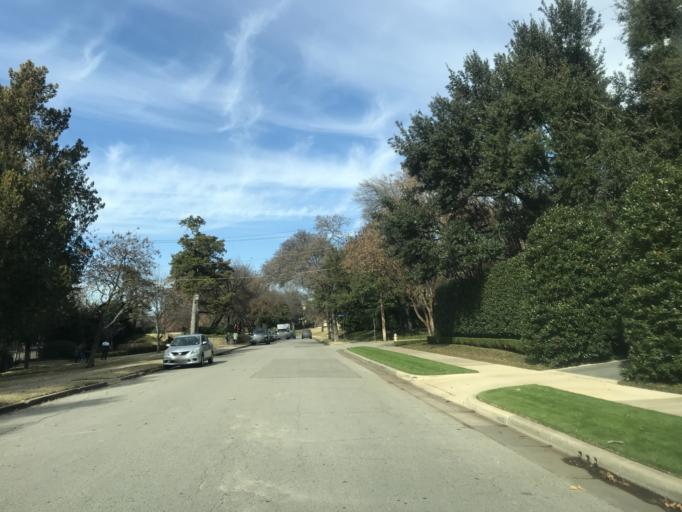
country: US
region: Texas
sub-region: Dallas County
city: Highland Park
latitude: 32.8262
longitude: -96.8008
